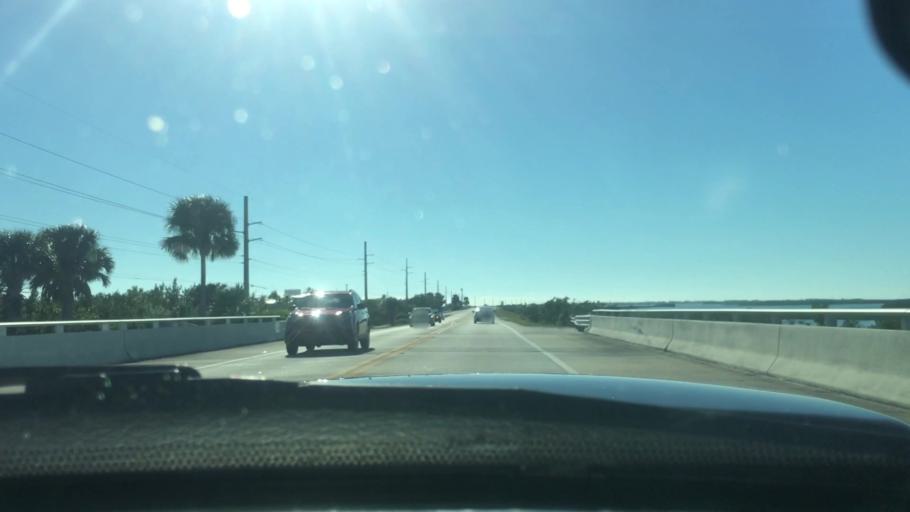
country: US
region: Florida
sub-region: Monroe County
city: Big Coppitt Key
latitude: 24.6267
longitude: -81.5978
